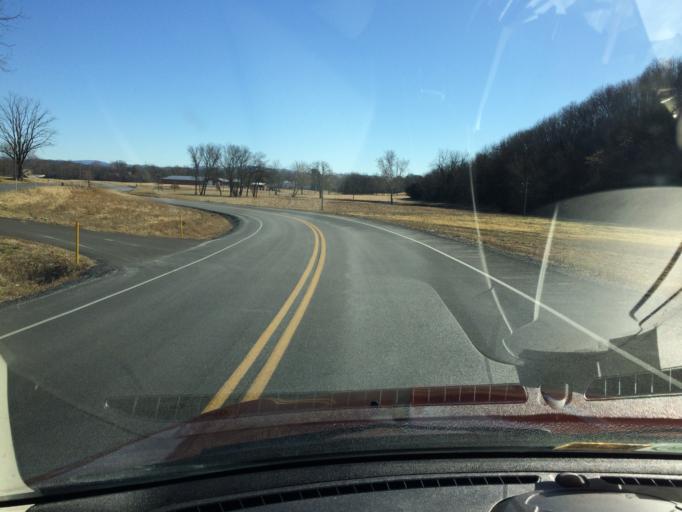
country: US
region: Virginia
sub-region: Rockingham County
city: Bridgewater
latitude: 38.3564
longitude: -78.9552
